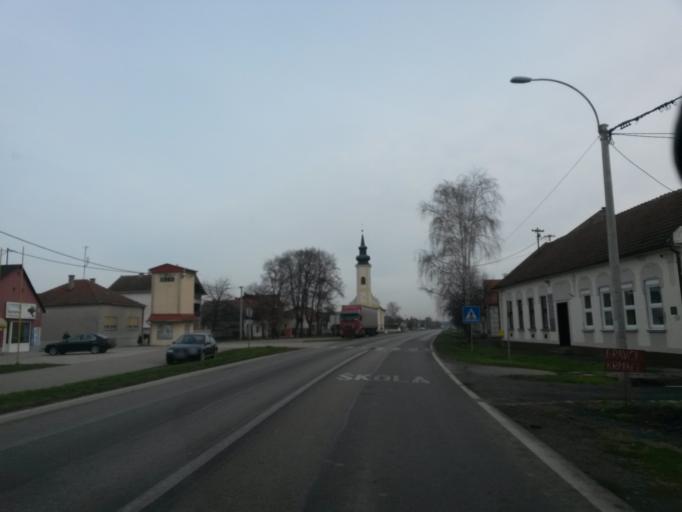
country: HR
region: Vukovarsko-Srijemska
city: Brsadin
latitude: 45.3609
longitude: 18.9044
